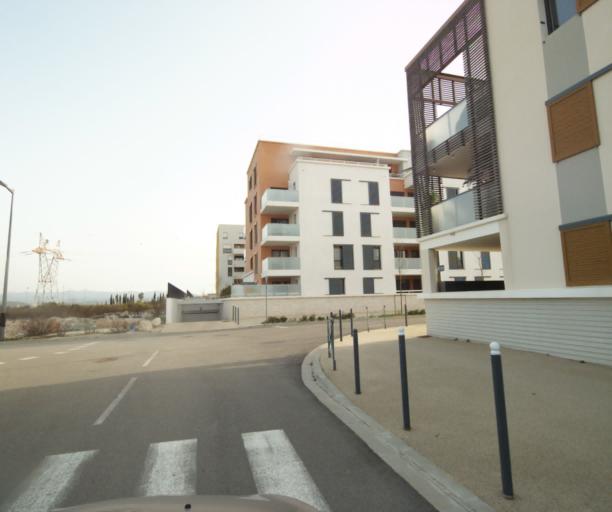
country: FR
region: Provence-Alpes-Cote d'Azur
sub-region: Departement des Bouches-du-Rhone
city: Cabries
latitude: 43.4844
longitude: 5.3490
